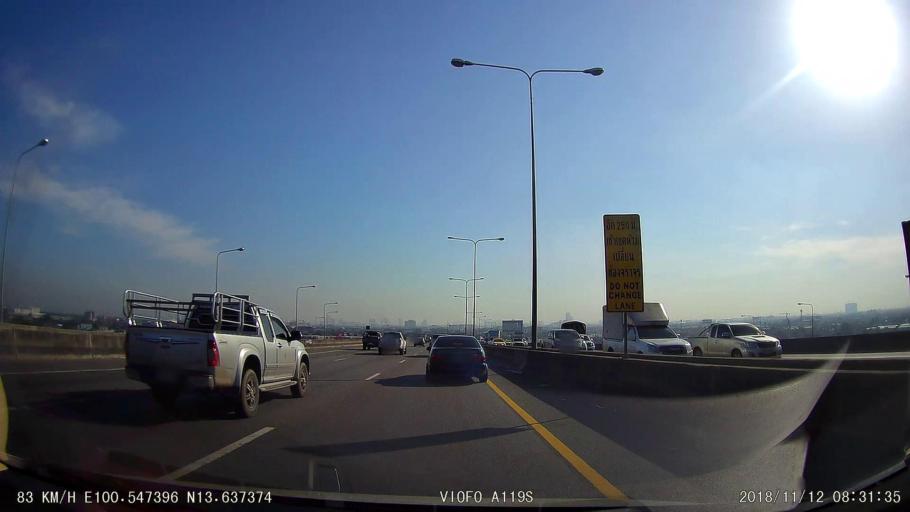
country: TH
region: Samut Prakan
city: Phra Pradaeng
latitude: 13.6377
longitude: 100.5482
